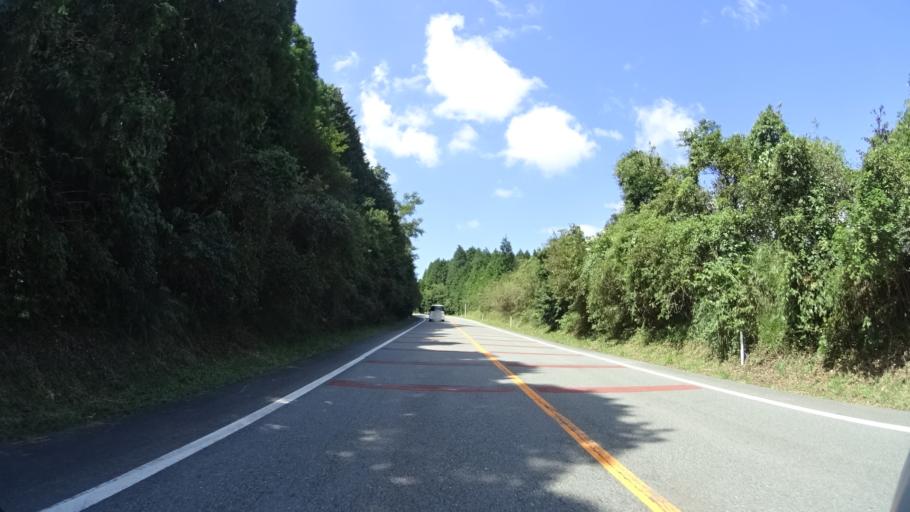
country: JP
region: Kumamoto
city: Aso
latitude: 33.0073
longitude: 131.1071
